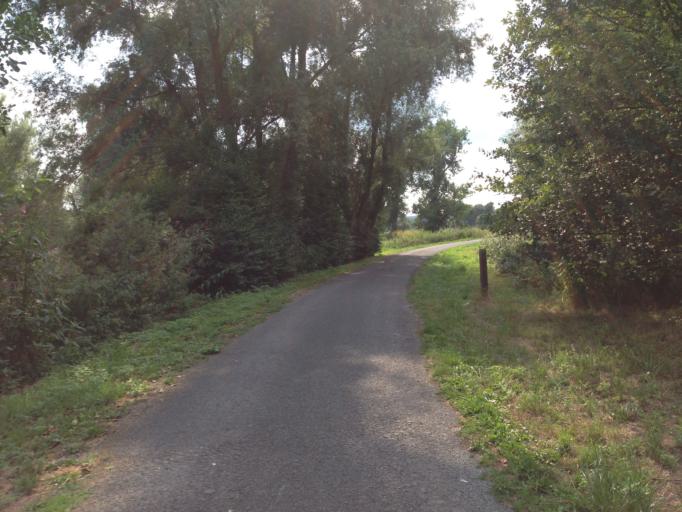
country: DE
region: Hesse
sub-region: Regierungsbezirk Giessen
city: Heuchelheim
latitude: 50.5703
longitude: 8.6365
